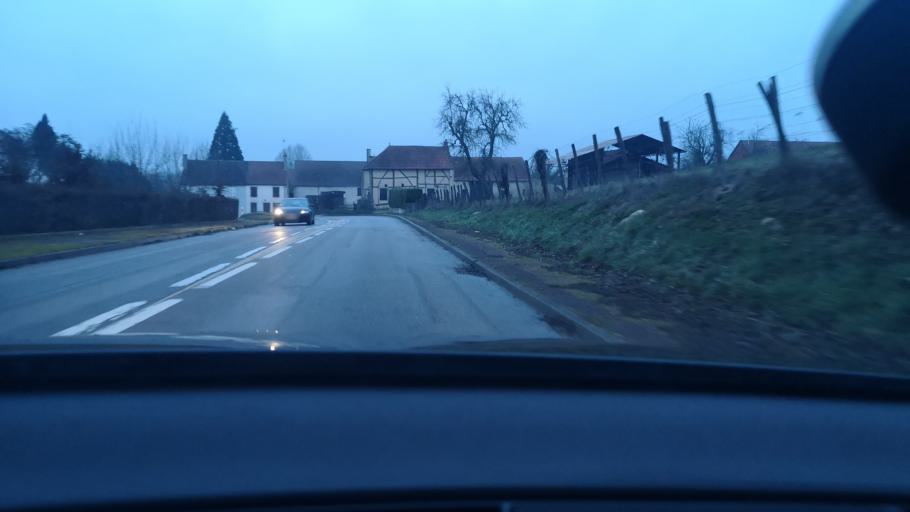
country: FR
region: Bourgogne
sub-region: Departement de Saone-et-Loire
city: Verdun-sur-le-Doubs
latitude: 47.0073
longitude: 4.9944
